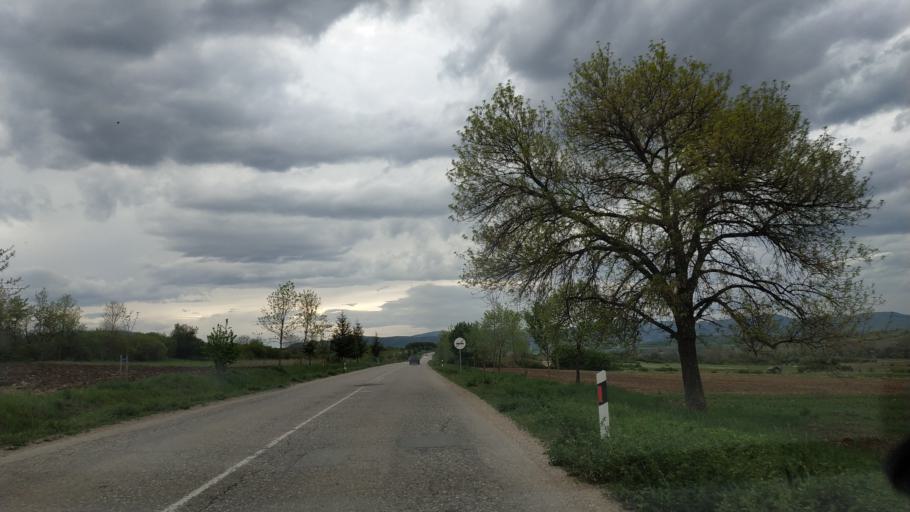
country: RS
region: Central Serbia
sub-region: Zajecarski Okrug
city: Soko Banja
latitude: 43.6533
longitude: 21.8411
